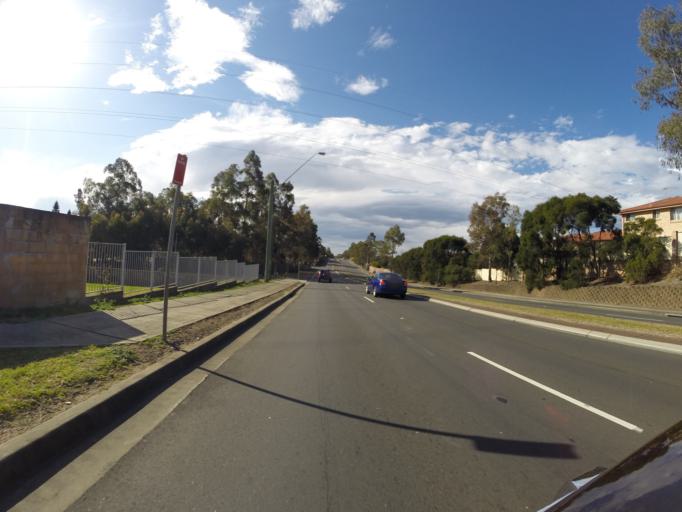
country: AU
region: New South Wales
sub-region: Fairfield
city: Cecil Park
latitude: -33.8803
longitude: 150.8663
